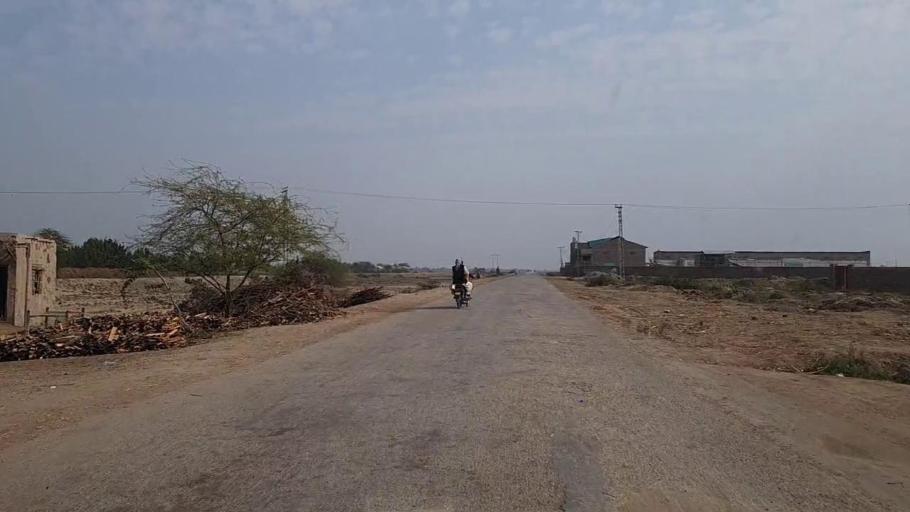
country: PK
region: Sindh
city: Mirpur Khas
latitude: 25.4268
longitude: 69.0176
